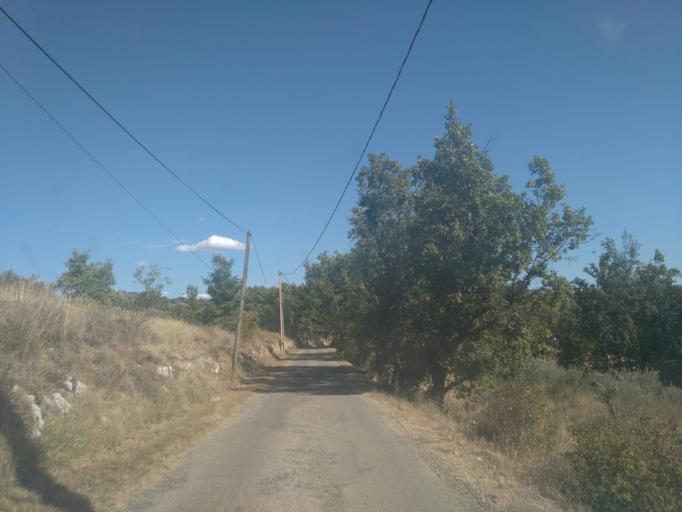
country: FR
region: Provence-Alpes-Cote d'Azur
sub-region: Departement du Var
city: Regusse
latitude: 43.7021
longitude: 6.1004
